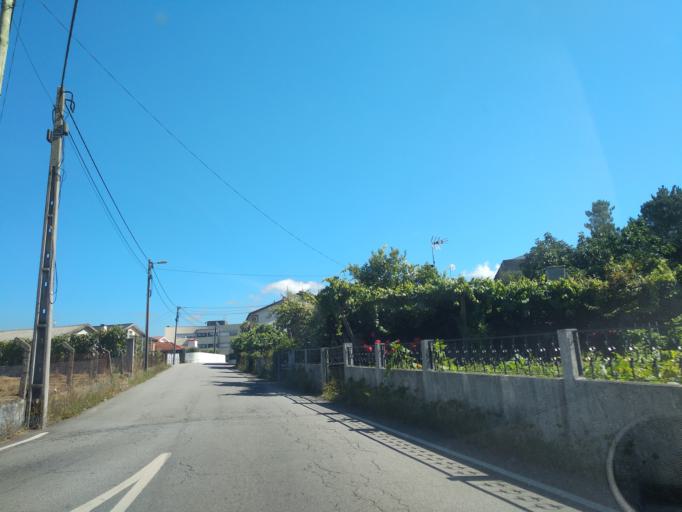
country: PT
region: Porto
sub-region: Pacos de Ferreira
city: Freamunde
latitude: 41.2759
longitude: -8.3348
